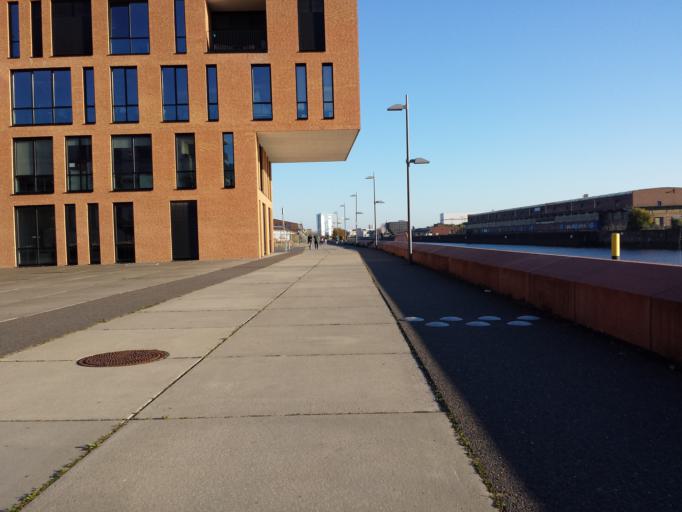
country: DE
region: Bremen
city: Bremen
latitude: 53.0945
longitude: 8.7653
